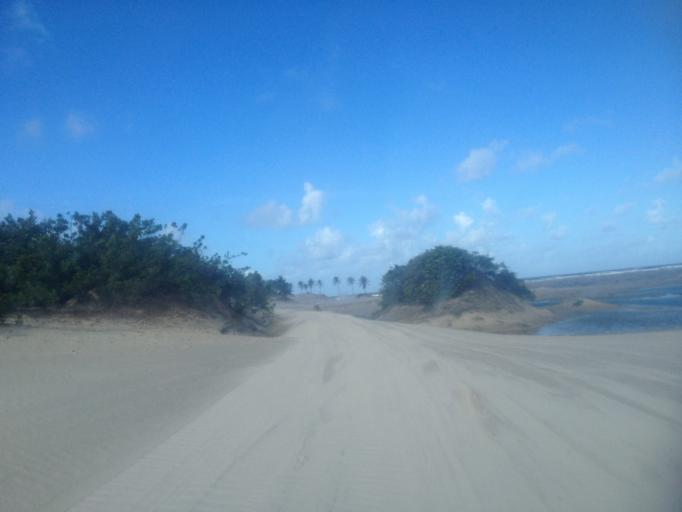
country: BR
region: Sergipe
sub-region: Indiaroba
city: Indiaroba
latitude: -11.4758
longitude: -37.3687
